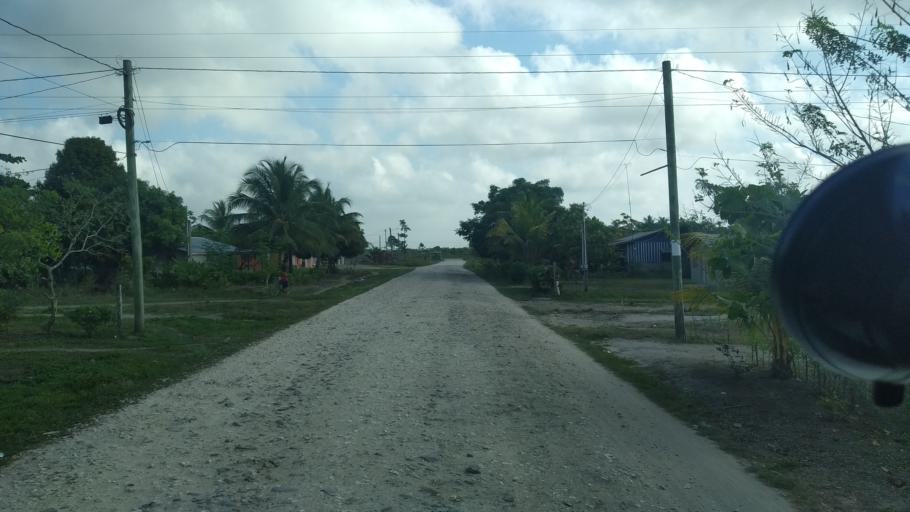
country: BZ
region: Stann Creek
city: Placencia
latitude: 16.5111
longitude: -88.5447
